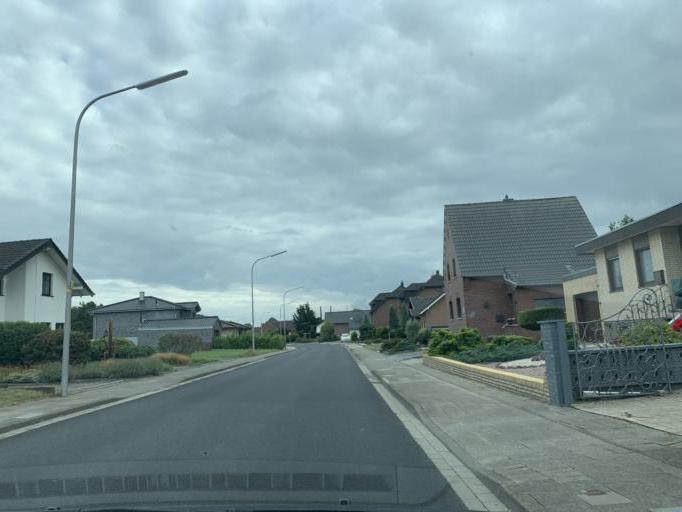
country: DE
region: North Rhine-Westphalia
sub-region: Regierungsbezirk Koln
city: Wassenberg
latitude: 51.0740
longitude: 6.1340
